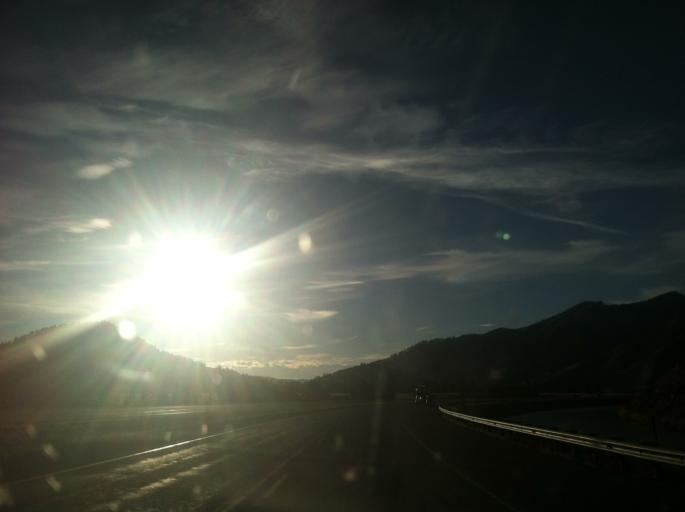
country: US
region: Montana
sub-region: Missoula County
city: Clinton
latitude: 46.6976
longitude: -113.3573
